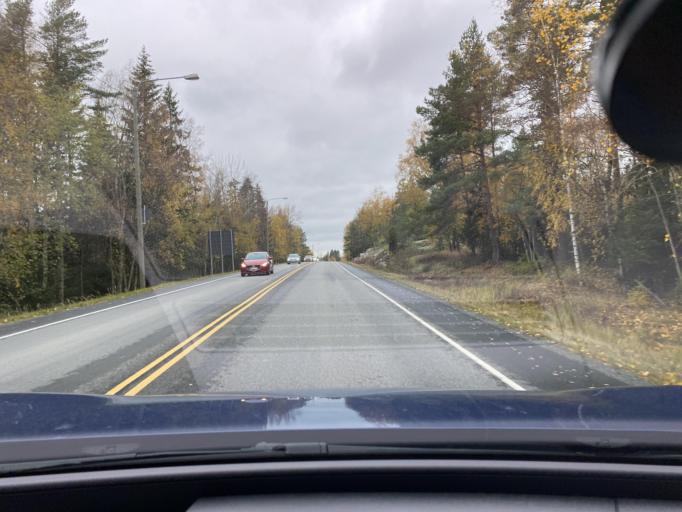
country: FI
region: Satakunta
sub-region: Rauma
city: Rauma
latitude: 61.1259
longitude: 21.6128
